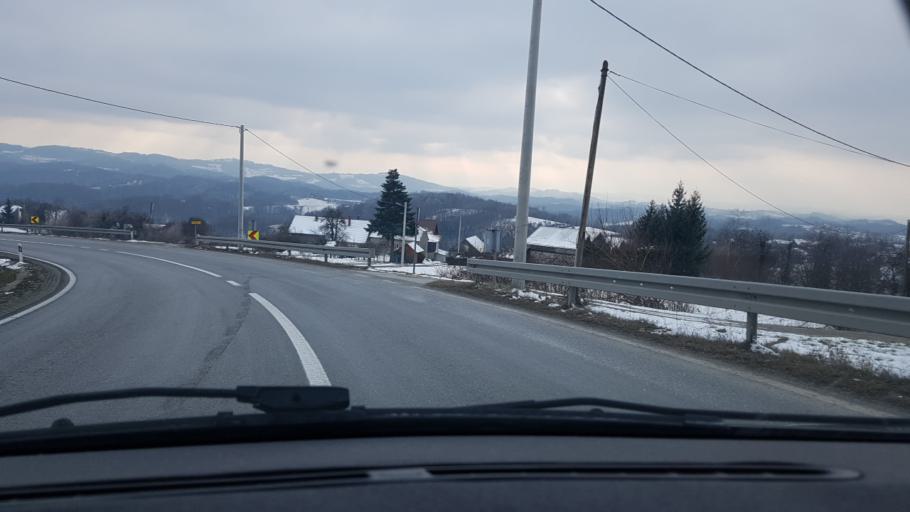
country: HR
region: Krapinsko-Zagorska
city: Mihovljan
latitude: 46.1616
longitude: 15.9607
